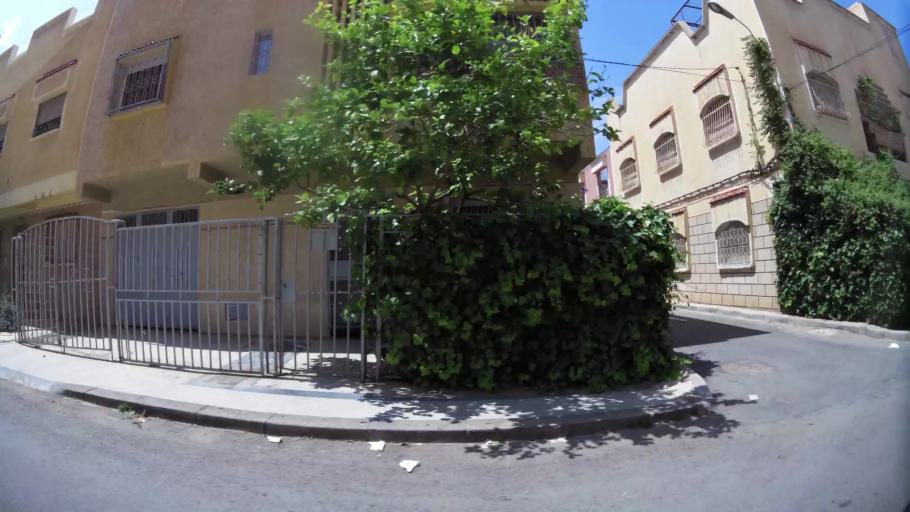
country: MA
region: Oriental
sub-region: Oujda-Angad
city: Oujda
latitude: 34.6886
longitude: -1.8856
